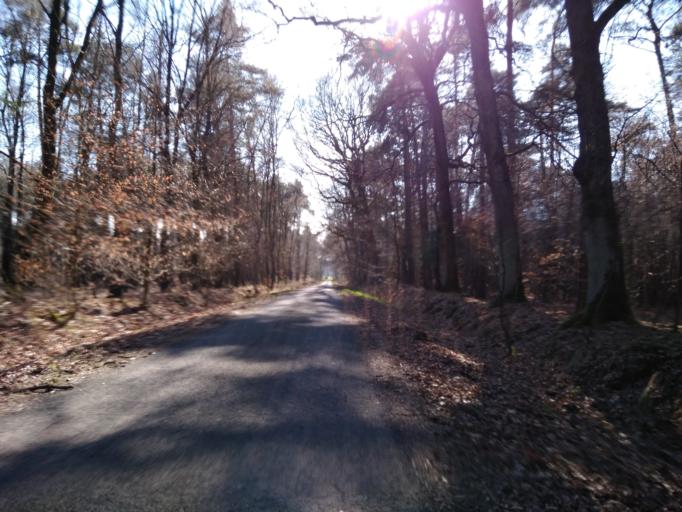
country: DE
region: North Rhine-Westphalia
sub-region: Regierungsbezirk Dusseldorf
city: Hunxe
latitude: 51.6438
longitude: 6.8324
